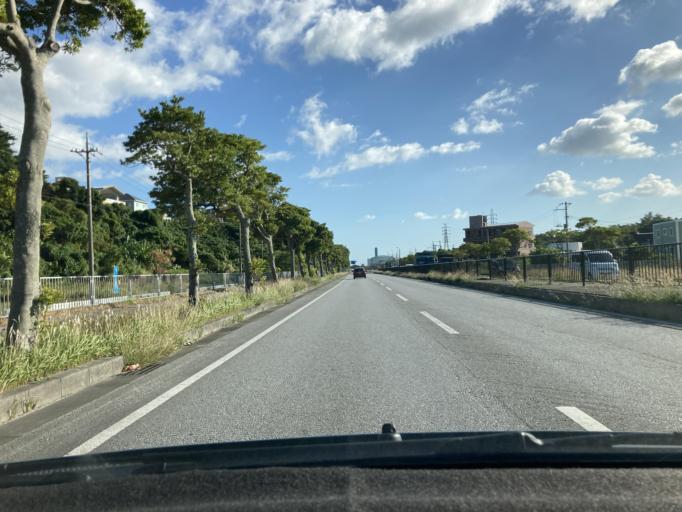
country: JP
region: Okinawa
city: Ishikawa
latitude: 26.4109
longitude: 127.8193
